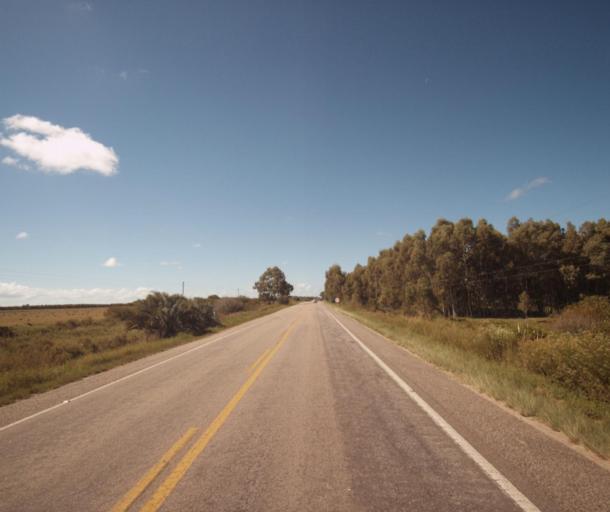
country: BR
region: Rio Grande do Sul
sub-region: Santa Vitoria Do Palmar
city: Santa Vitoria do Palmar
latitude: -33.5706
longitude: -53.3753
